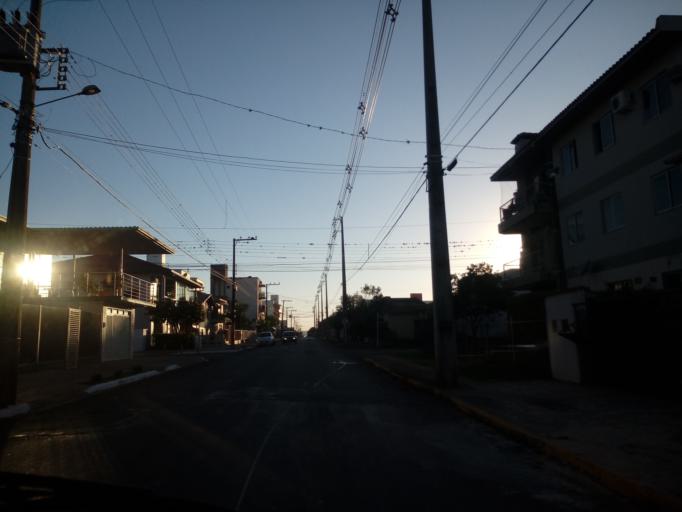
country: BR
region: Santa Catarina
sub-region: Chapeco
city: Chapeco
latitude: -27.0883
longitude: -52.6311
